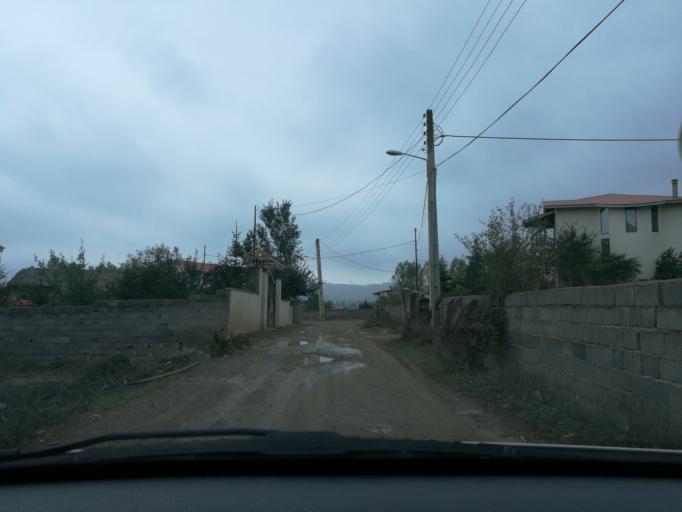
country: IR
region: Mazandaran
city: `Abbasabad
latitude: 36.5054
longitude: 51.1977
